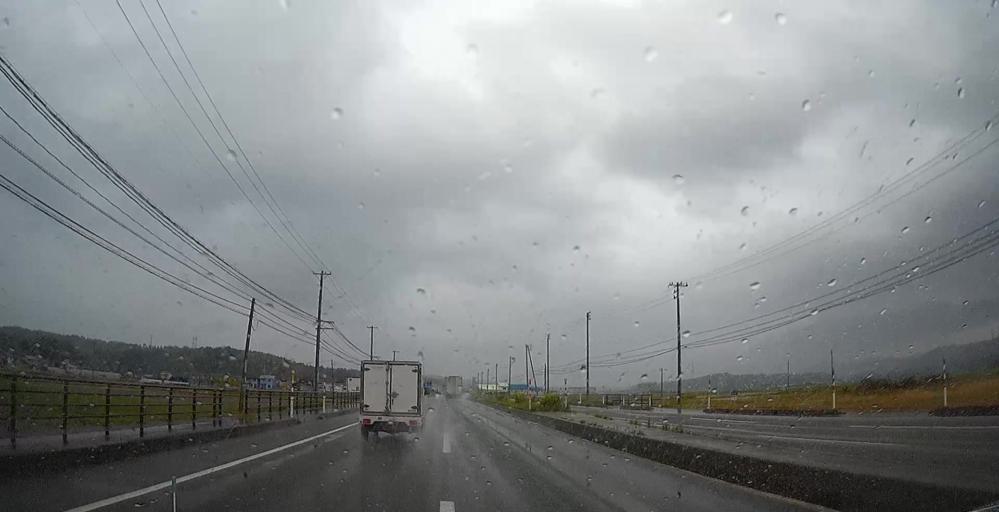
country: JP
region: Niigata
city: Kashiwazaki
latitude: 37.4263
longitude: 138.6211
